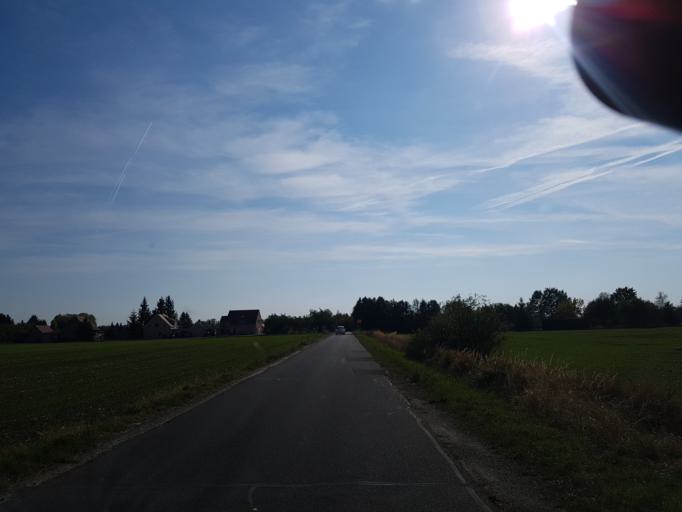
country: DE
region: Brandenburg
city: Doberlug-Kirchhain
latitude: 51.6429
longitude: 13.5478
